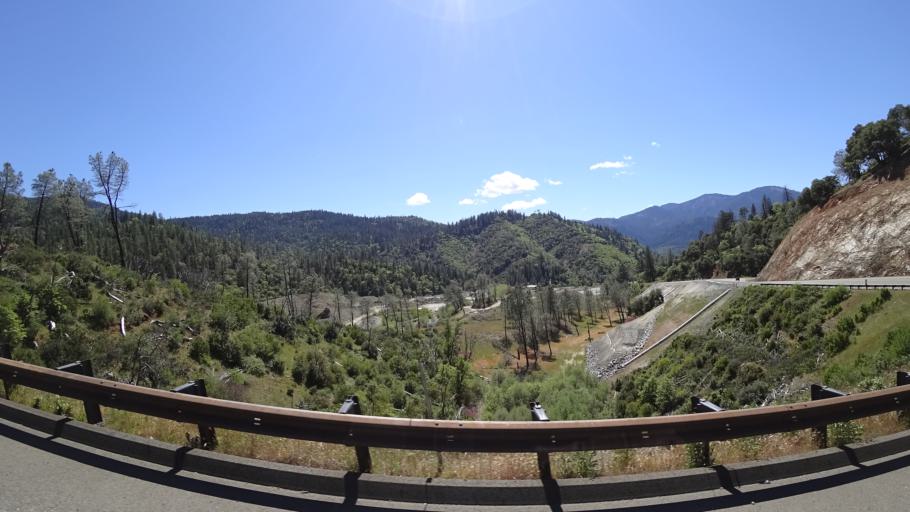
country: US
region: California
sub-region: Trinity County
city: Weaverville
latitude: 40.7360
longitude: -123.0128
